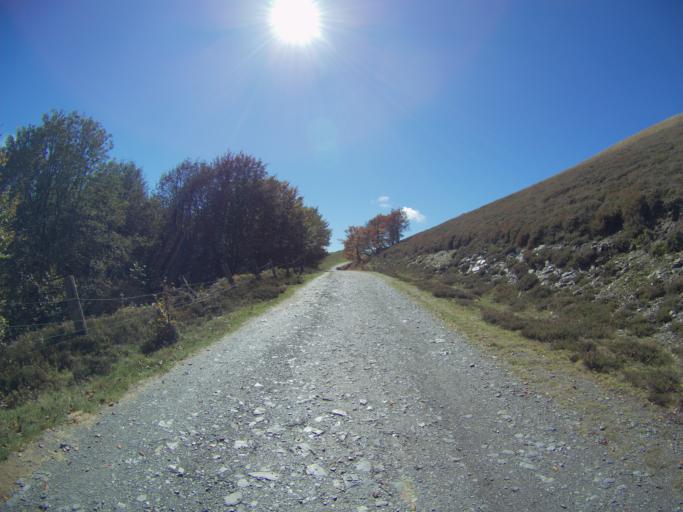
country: ES
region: Navarre
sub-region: Provincia de Navarra
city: Garralda
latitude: 43.0289
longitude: -1.2961
